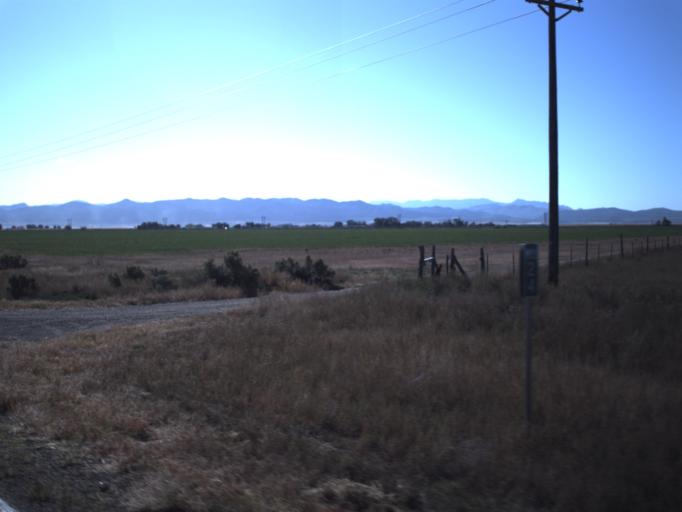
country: US
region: Utah
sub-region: Washington County
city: Enterprise
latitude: 37.7161
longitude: -113.6747
